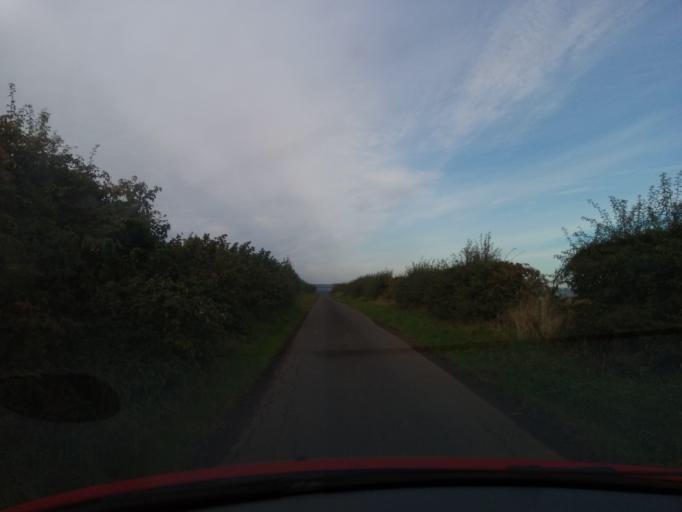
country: GB
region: Scotland
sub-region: The Scottish Borders
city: Kelso
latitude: 55.5874
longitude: -2.3767
